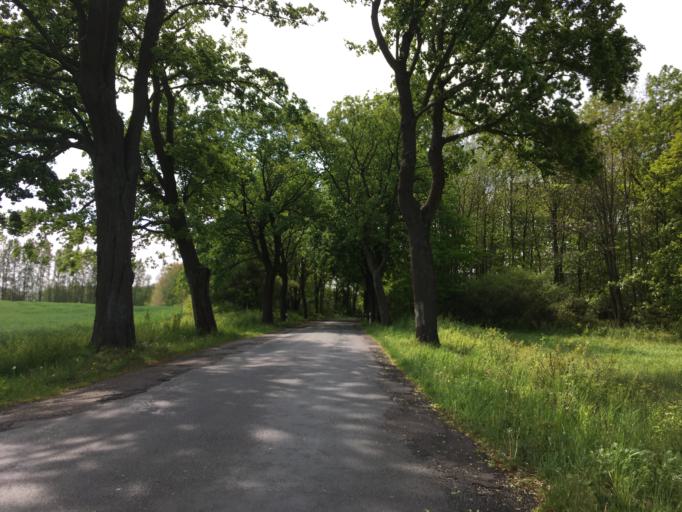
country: DE
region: Brandenburg
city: Melchow
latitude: 52.7476
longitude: 13.6853
